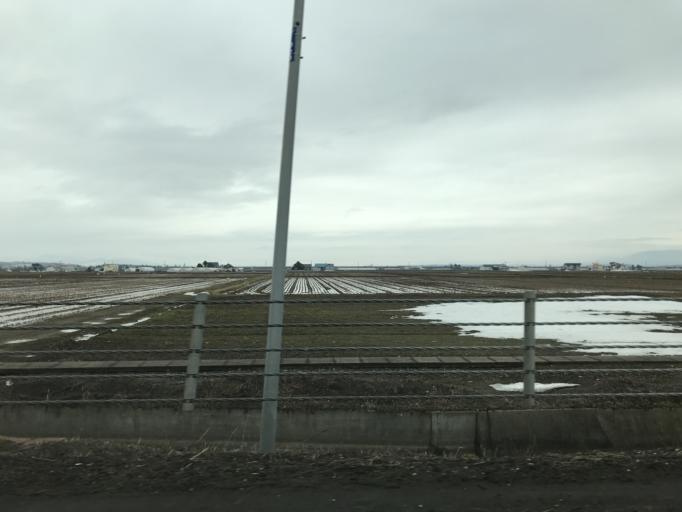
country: JP
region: Hokkaido
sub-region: Asahikawa-shi
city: Asahikawa
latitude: 43.8309
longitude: 142.4245
